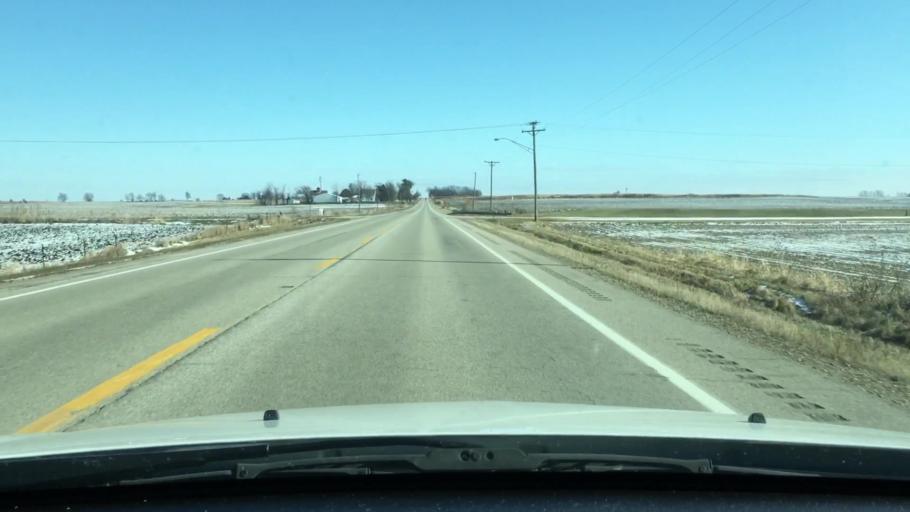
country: US
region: Illinois
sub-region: DeKalb County
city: Malta
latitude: 42.0008
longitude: -88.9183
